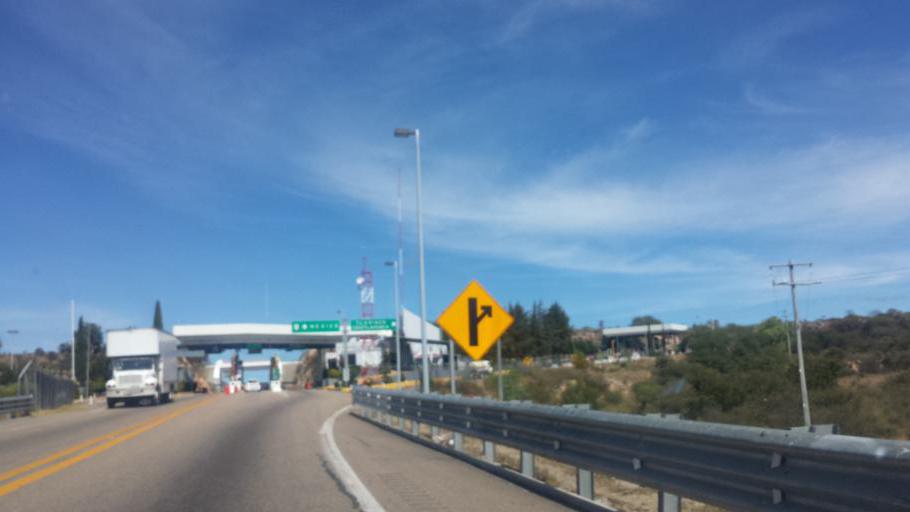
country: MX
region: Oaxaca
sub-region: Villa Tejupam de la Union
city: Villa Tejupam de la Union
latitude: 17.7247
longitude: -97.3532
